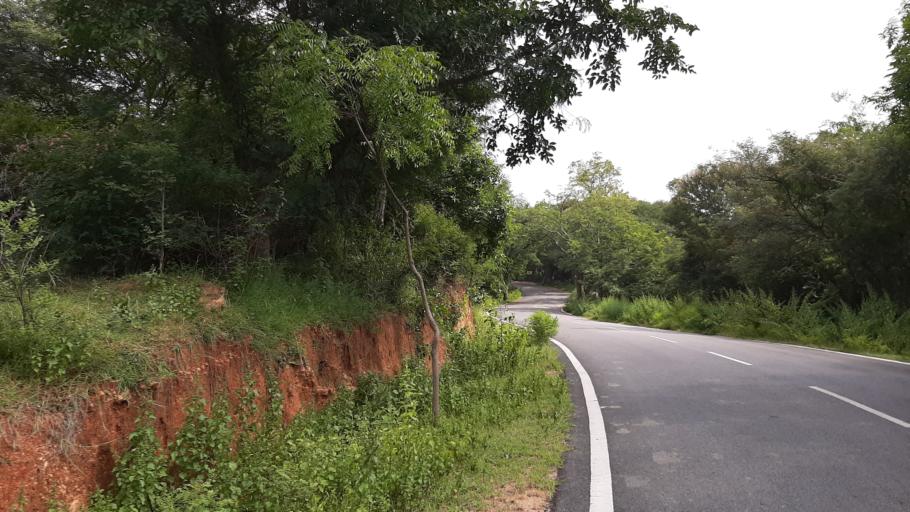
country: IN
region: Karnataka
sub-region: Ramanagara
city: Magadi
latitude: 12.9039
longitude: 77.2906
